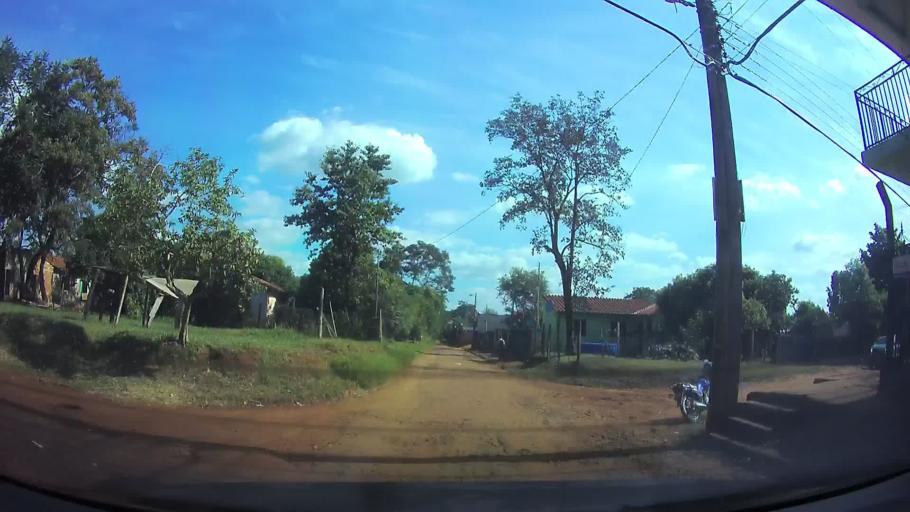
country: PY
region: Central
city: Limpio
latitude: -25.2456
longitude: -57.4676
